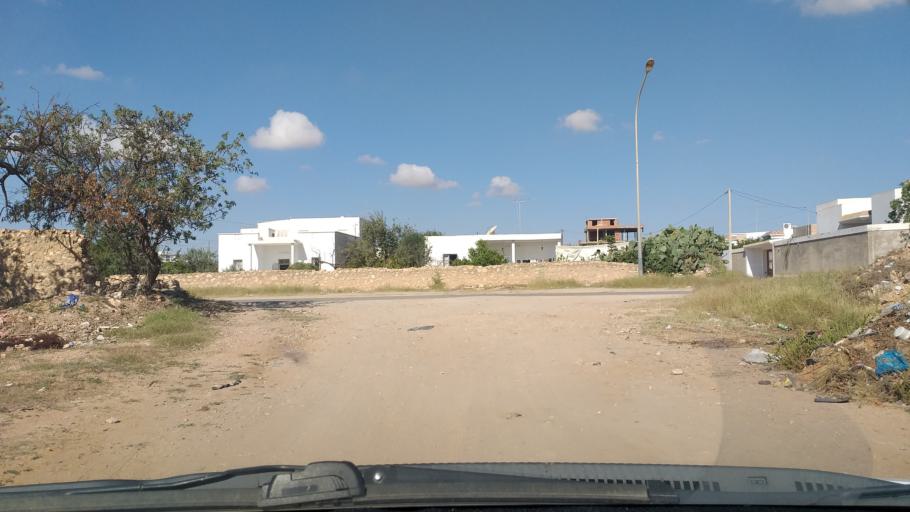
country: TN
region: Safaqis
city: Al Qarmadah
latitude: 34.8025
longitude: 10.7677
